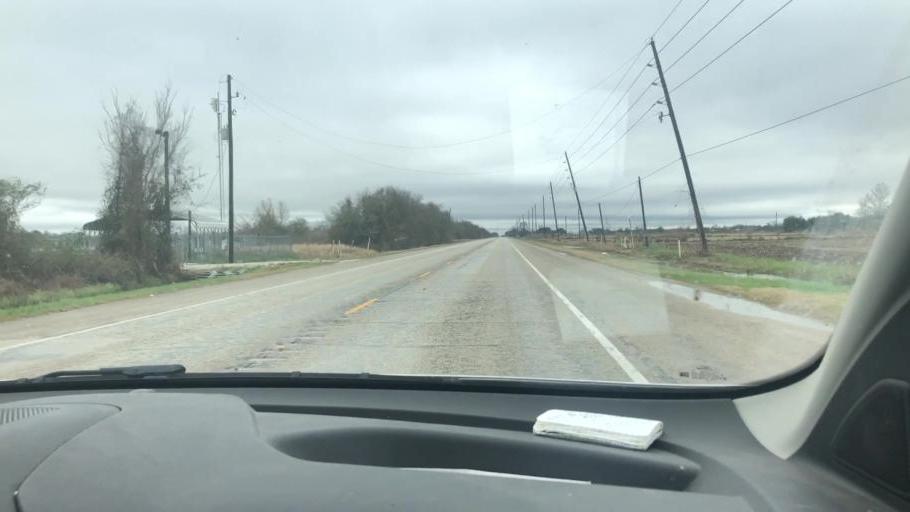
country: US
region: Texas
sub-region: Wharton County
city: Wharton
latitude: 29.2788
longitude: -96.0651
